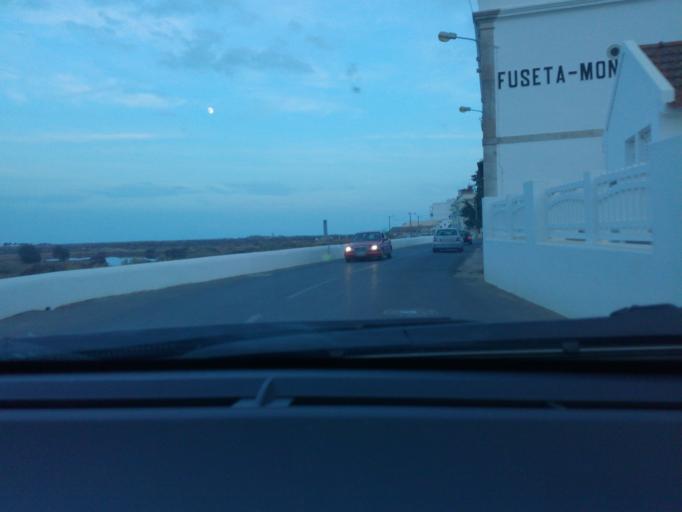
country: PT
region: Faro
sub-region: Olhao
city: Laranjeiro
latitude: 37.0605
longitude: -7.7519
